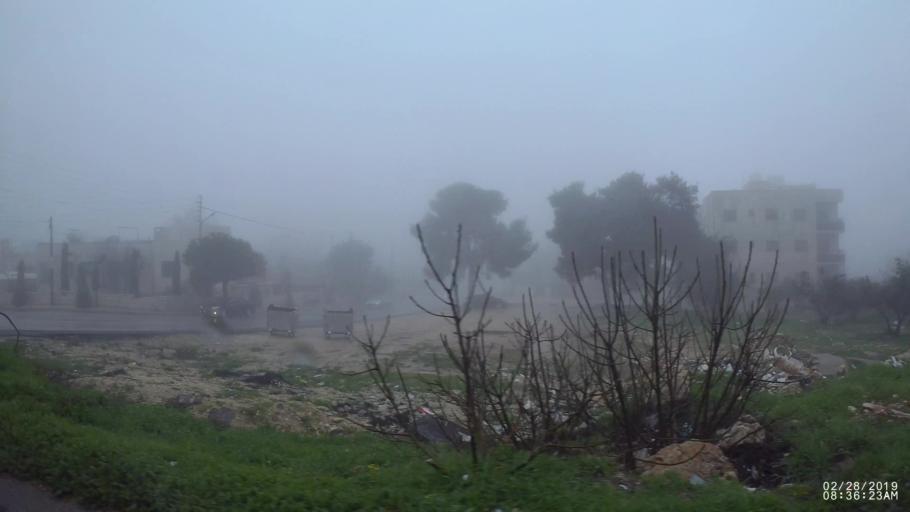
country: JO
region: Amman
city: Al Jubayhah
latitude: 32.0139
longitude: 35.8806
